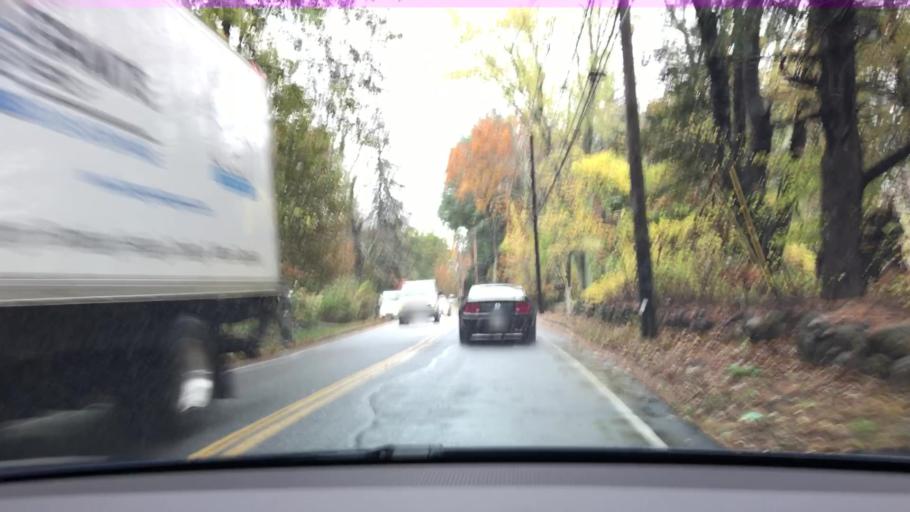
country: US
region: Massachusetts
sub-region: Middlesex County
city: Billerica
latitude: 42.5339
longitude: -71.2847
